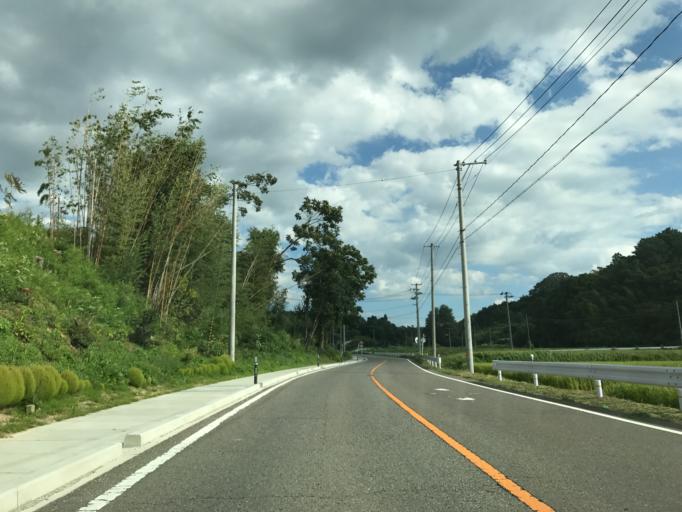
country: JP
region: Fukushima
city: Koriyama
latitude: 37.4066
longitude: 140.4356
